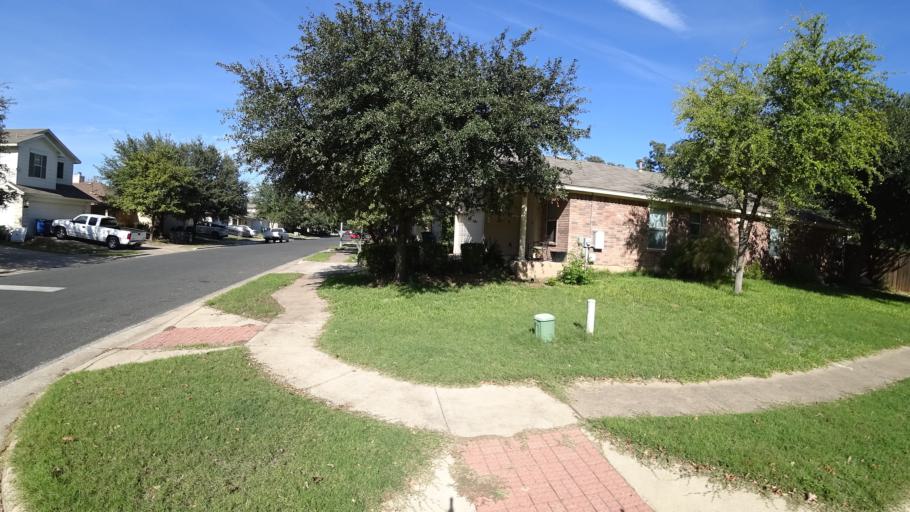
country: US
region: Texas
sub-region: Travis County
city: Austin
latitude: 30.2577
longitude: -97.6864
